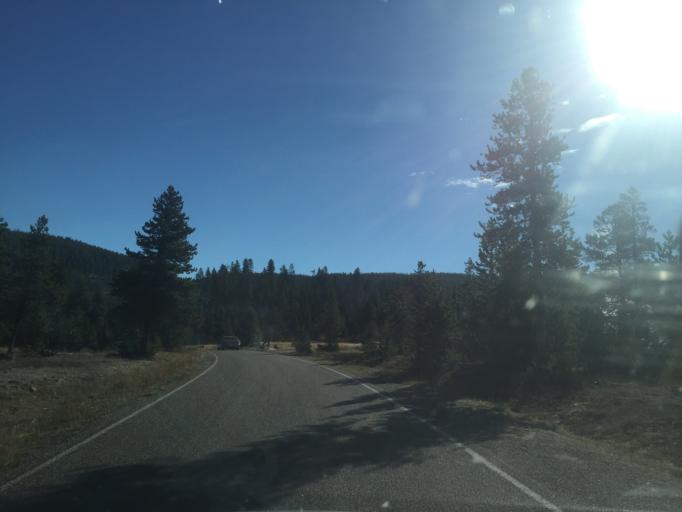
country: US
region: Montana
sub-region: Gallatin County
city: West Yellowstone
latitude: 44.5426
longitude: -110.7894
